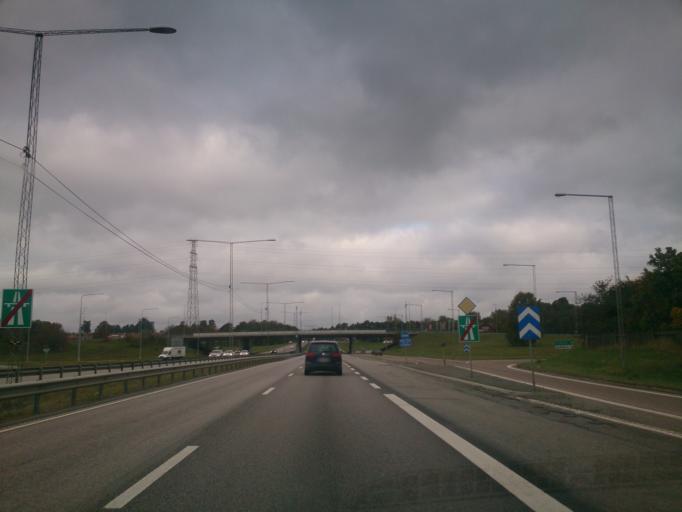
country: SE
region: Stockholm
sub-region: Stockholms Kommun
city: Arsta
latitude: 59.2587
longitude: 18.1001
